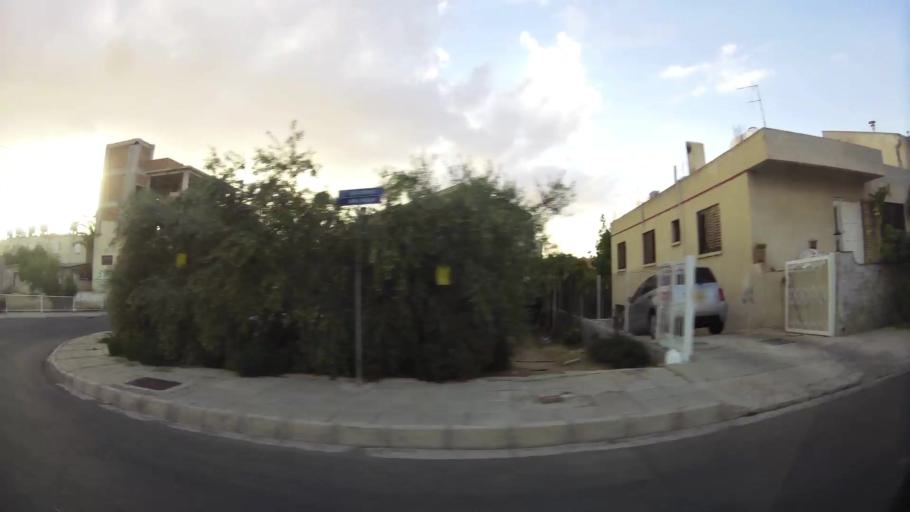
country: CY
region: Lefkosia
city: Tseri
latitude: 35.1157
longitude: 33.3182
